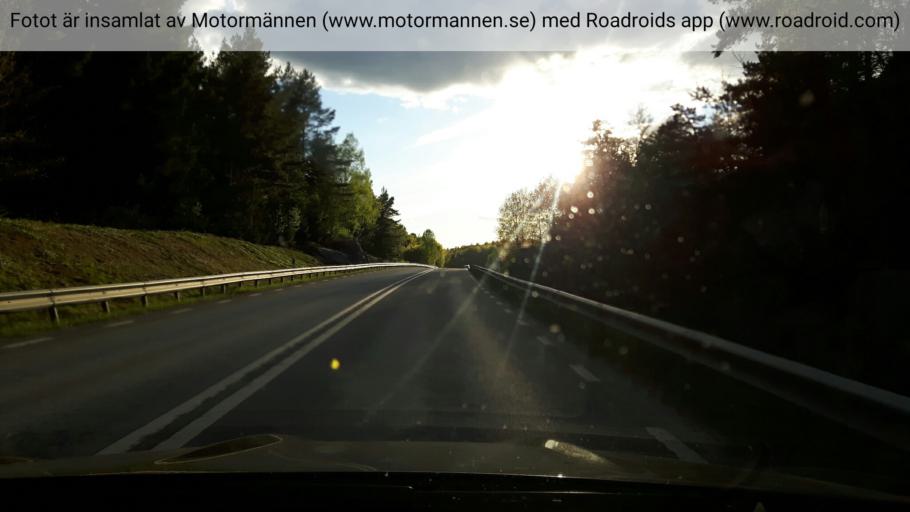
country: SE
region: Stockholm
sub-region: Vaxholms Kommun
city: Resaro
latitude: 59.4240
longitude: 18.2818
